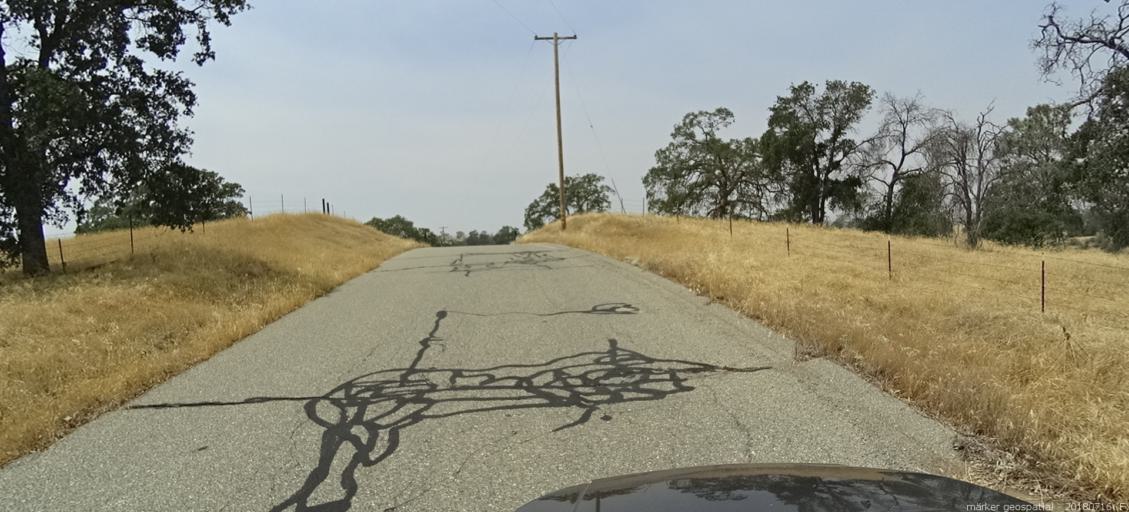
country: US
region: California
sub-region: Madera County
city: Yosemite Lakes
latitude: 37.1918
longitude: -119.9065
